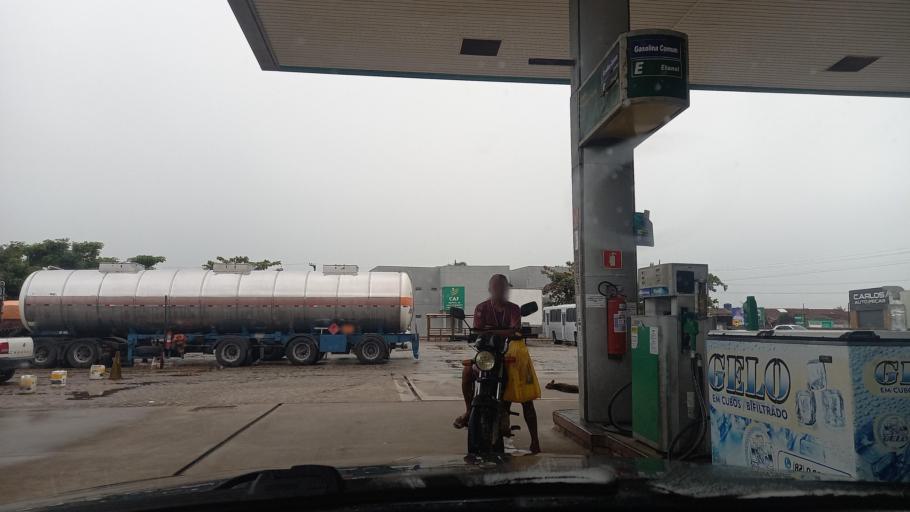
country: BR
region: Alagoas
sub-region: Campo Alegre
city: Campo Alegre
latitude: -9.7794
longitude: -36.3519
